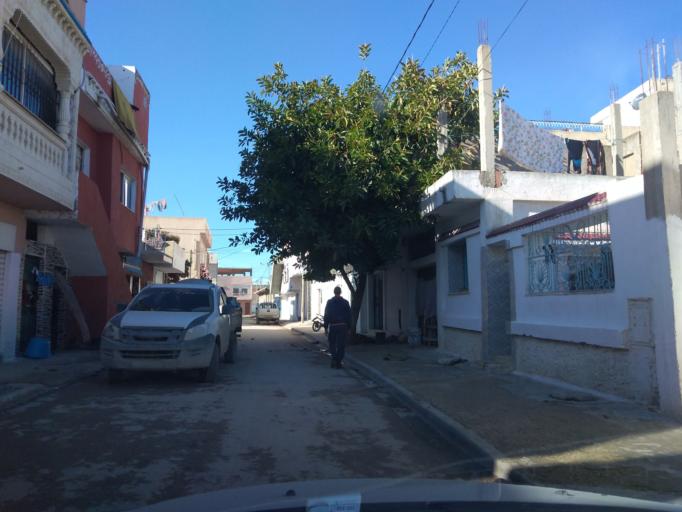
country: TN
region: Ariana
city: Qal'at al Andalus
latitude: 37.0658
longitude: 10.1221
